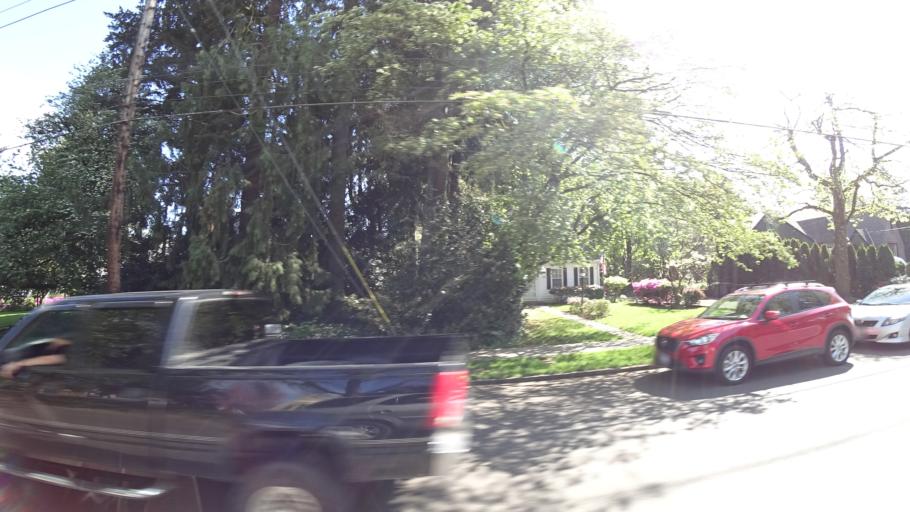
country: US
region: Oregon
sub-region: Washington County
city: Hillsboro
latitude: 45.5223
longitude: -122.9761
